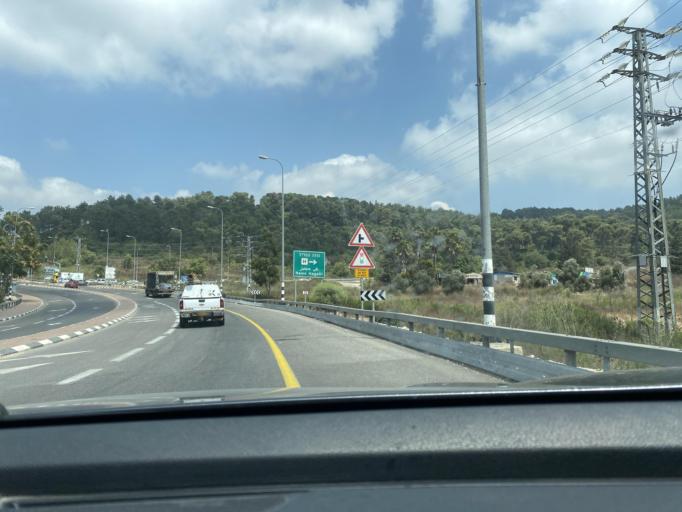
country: IL
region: Northern District
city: Kefar Weradim
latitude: 33.0038
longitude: 35.2942
